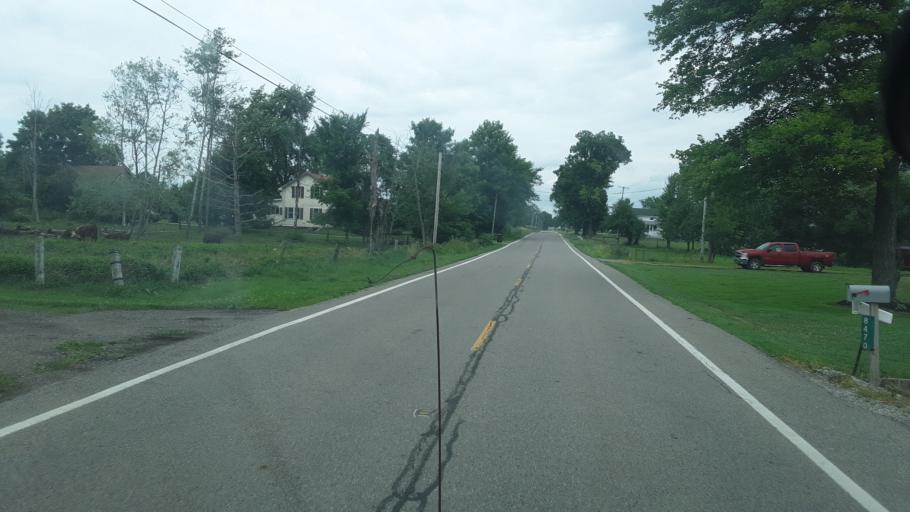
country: US
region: Ohio
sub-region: Trumbull County
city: Cortland
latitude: 41.4510
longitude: -80.6656
